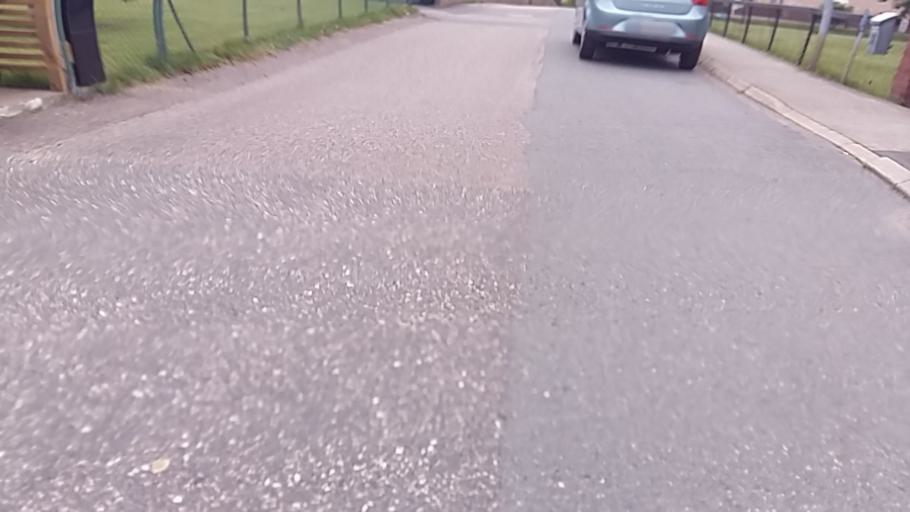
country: SE
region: Joenkoeping
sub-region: Jonkopings Kommun
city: Odensjo
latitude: 57.7138
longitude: 14.1227
